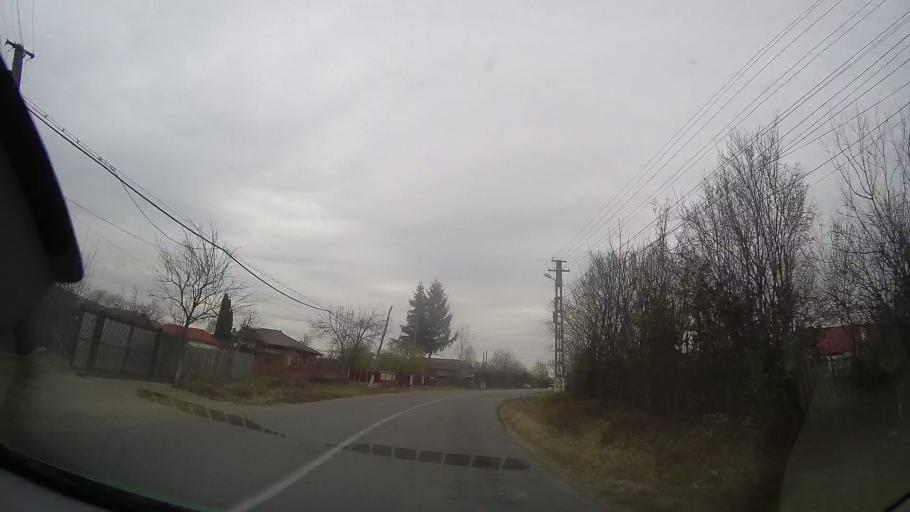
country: RO
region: Prahova
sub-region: Comuna Iordachianu
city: Iordacheanu
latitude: 45.0405
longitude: 26.2373
